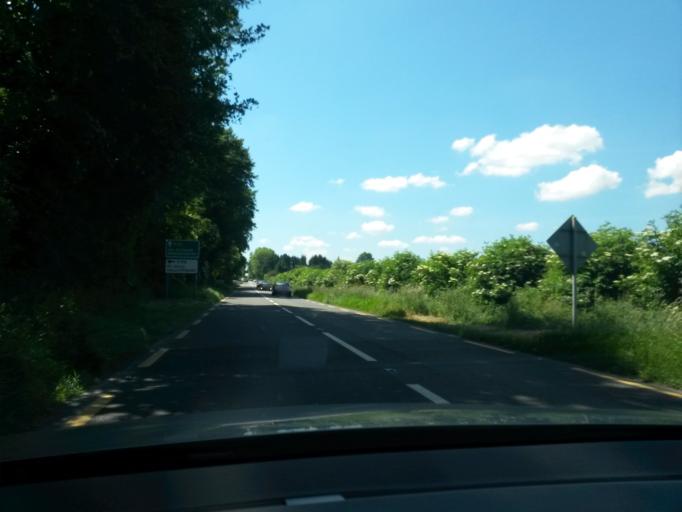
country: IE
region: Leinster
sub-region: Wicklow
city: Blessington
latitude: 53.1530
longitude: -6.5541
